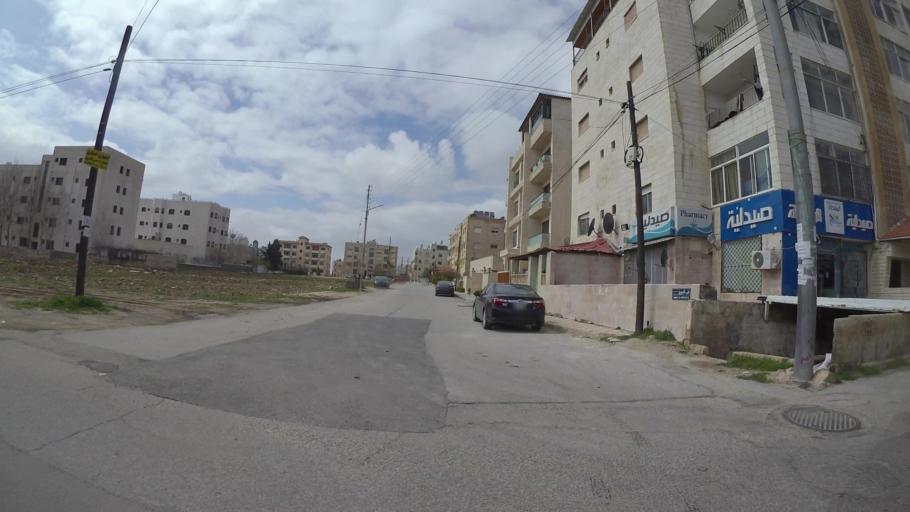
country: JO
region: Amman
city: Wadi as Sir
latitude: 31.9639
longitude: 35.8386
